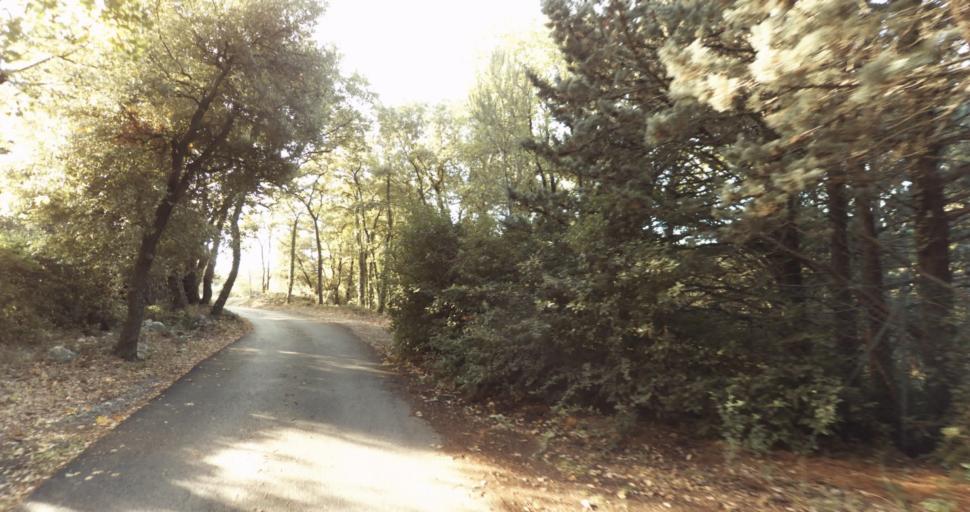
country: FR
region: Provence-Alpes-Cote d'Azur
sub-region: Departement des Bouches-du-Rhone
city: Venelles
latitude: 43.5985
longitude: 5.4729
